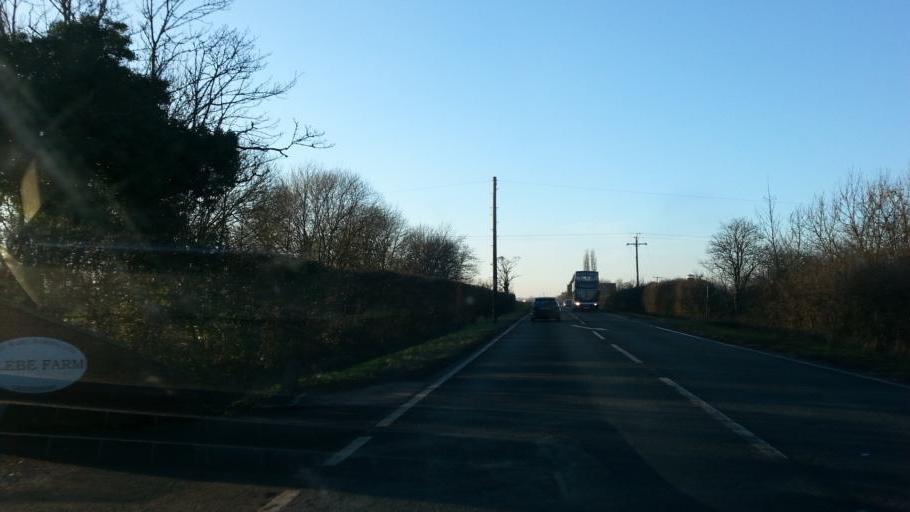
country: GB
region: England
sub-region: Lincolnshire
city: Navenby
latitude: 53.0660
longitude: -0.6215
